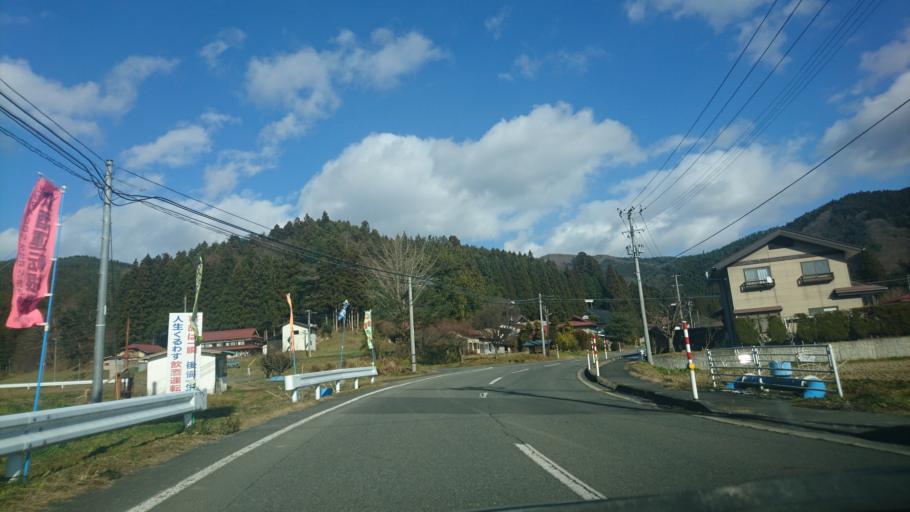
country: JP
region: Iwate
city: Mizusawa
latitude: 39.0738
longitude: 141.3829
